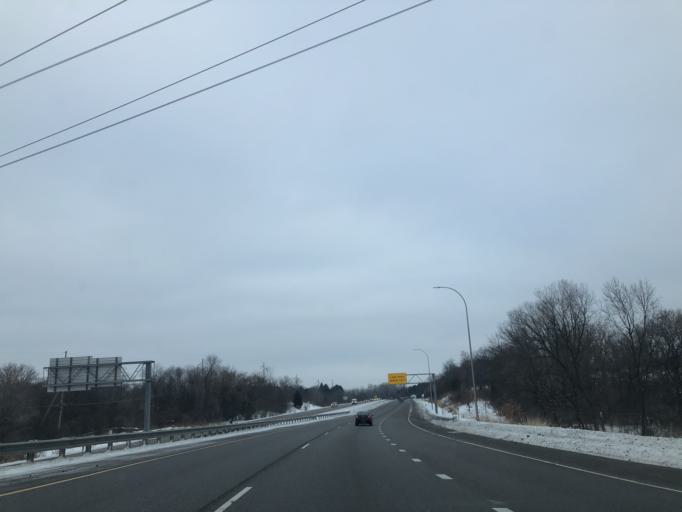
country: US
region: Minnesota
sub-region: Ramsey County
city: Arden Hills
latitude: 45.0681
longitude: -93.1668
